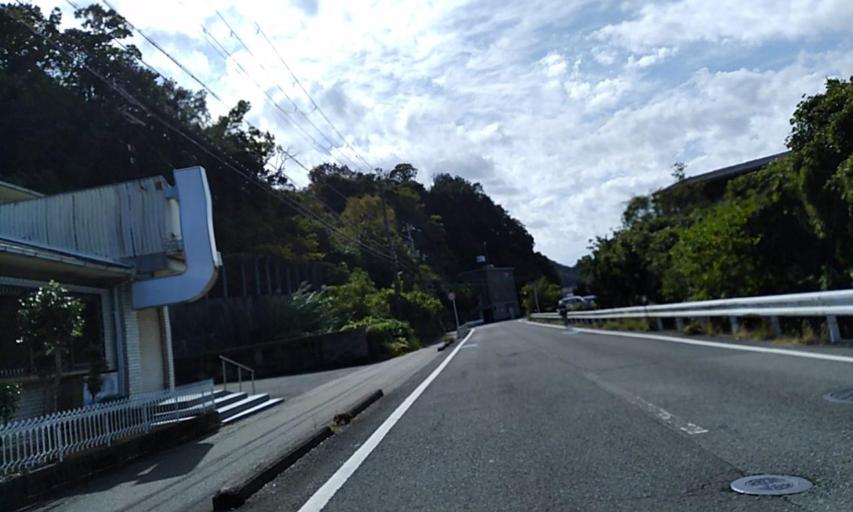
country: JP
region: Wakayama
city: Gobo
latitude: 33.9622
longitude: 135.1138
